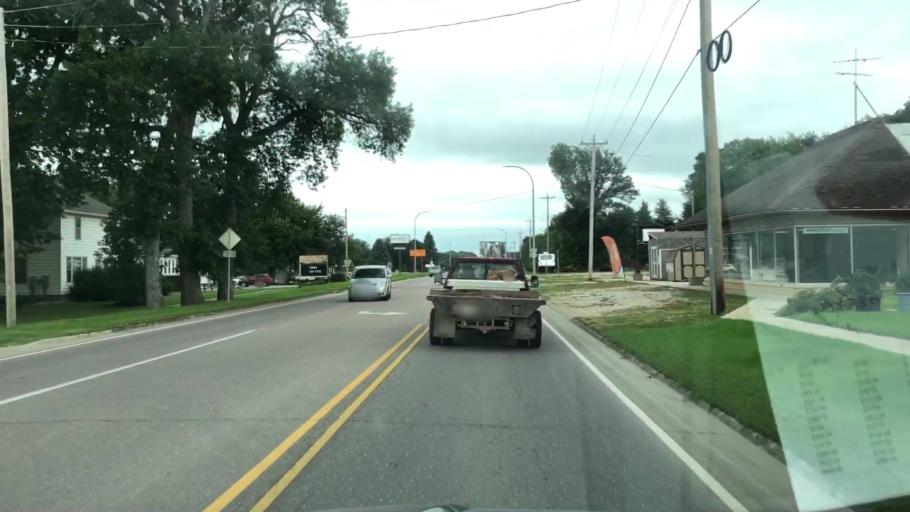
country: US
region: Iowa
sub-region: O'Brien County
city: Sheldon
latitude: 43.1860
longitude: -95.8417
